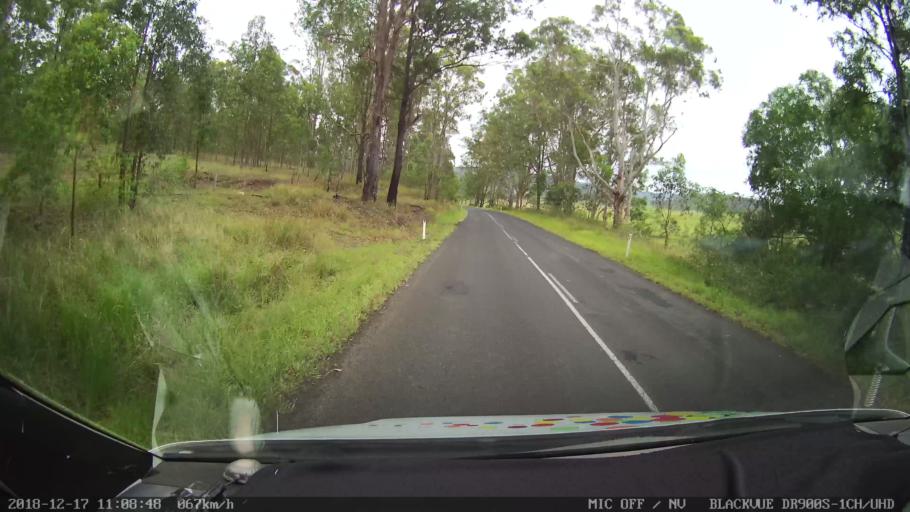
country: AU
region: New South Wales
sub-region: Kyogle
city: Kyogle
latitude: -28.7601
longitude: 152.6553
